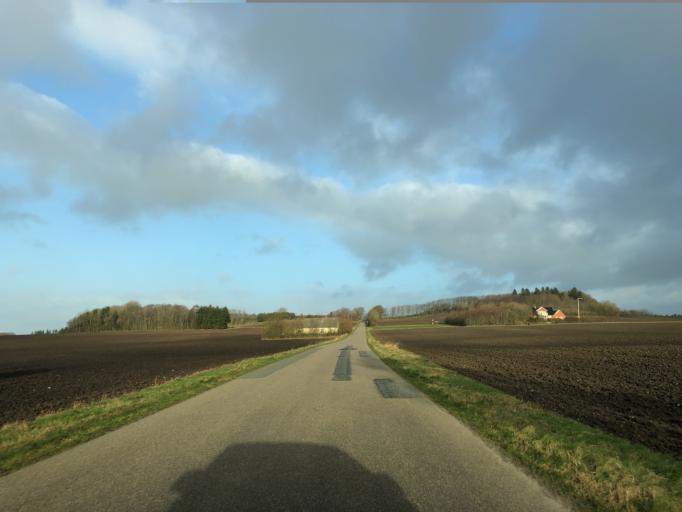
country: DK
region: Central Jutland
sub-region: Ringkobing-Skjern Kommune
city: Videbaek
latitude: 56.1838
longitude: 8.5410
